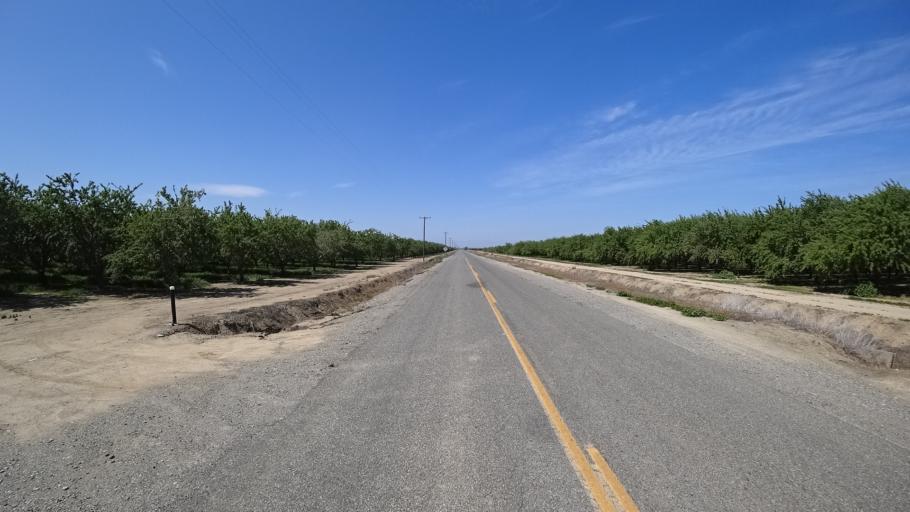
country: US
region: California
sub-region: Glenn County
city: Hamilton City
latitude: 39.6525
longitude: -122.0665
